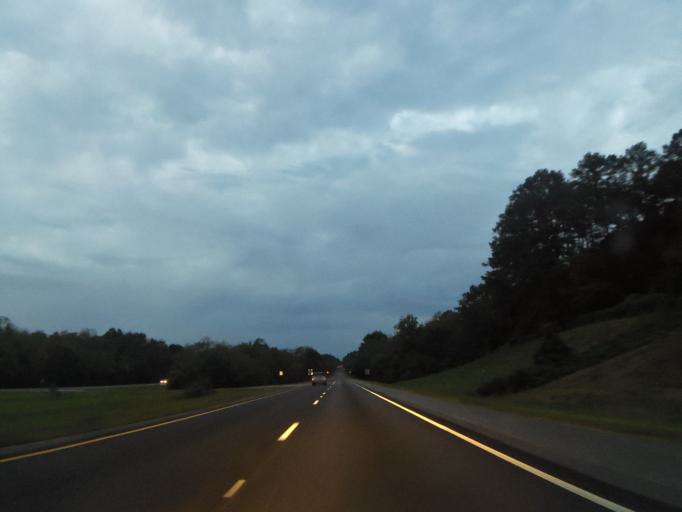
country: US
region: Alabama
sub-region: DeKalb County
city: Crossville
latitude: 34.1938
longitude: -85.9492
